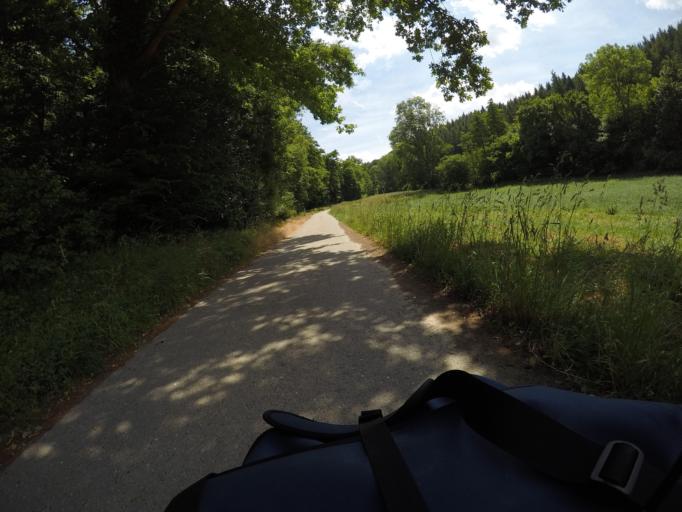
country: DE
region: Baden-Wuerttemberg
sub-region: Regierungsbezirk Stuttgart
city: Ittlingen
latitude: 49.2146
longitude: 8.9403
